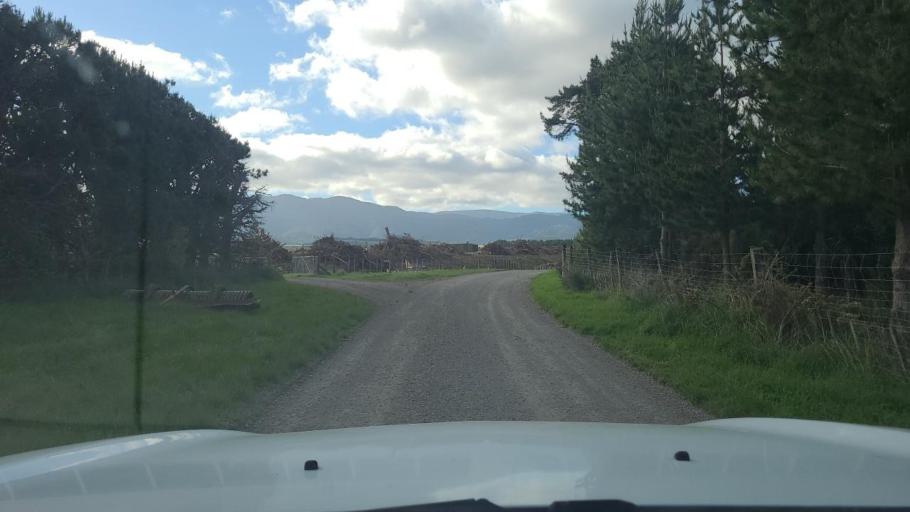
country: NZ
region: Wellington
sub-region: Upper Hutt City
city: Upper Hutt
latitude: -41.3440
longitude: 175.2294
